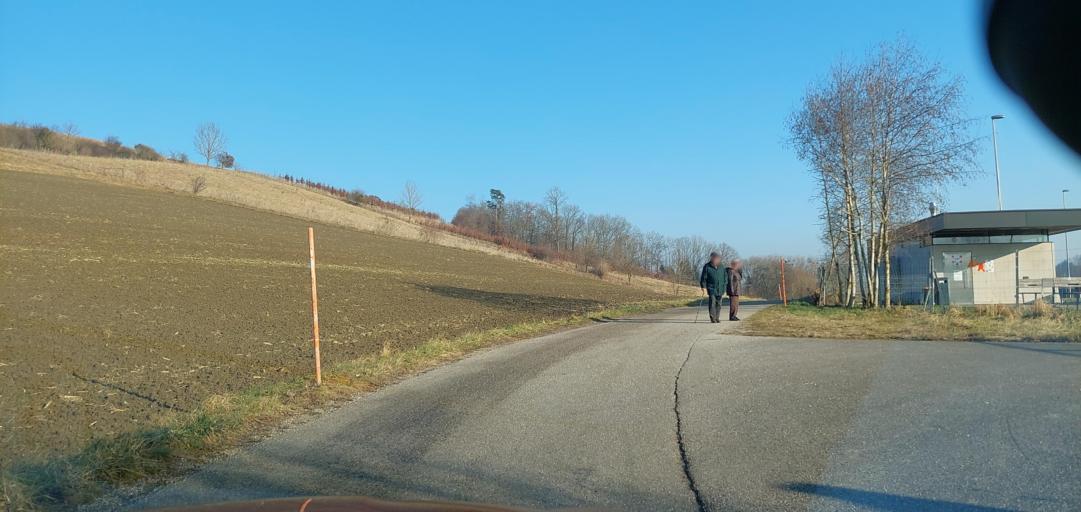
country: AT
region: Upper Austria
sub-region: Wels-Land
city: Offenhausen
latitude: 48.1801
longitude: 13.8600
